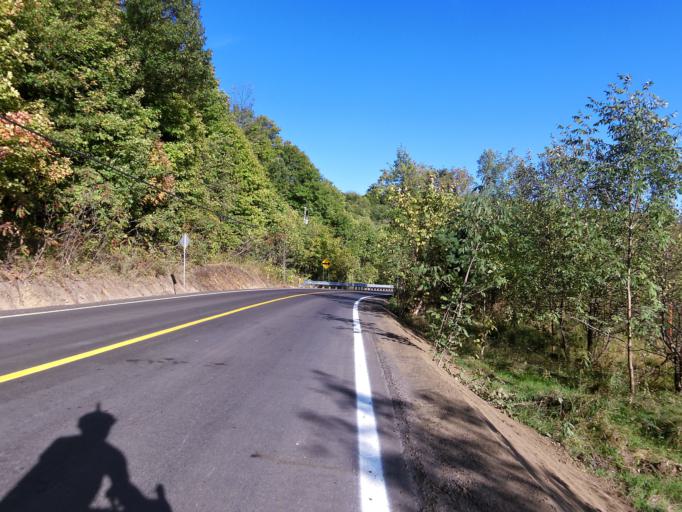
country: CA
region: Quebec
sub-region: Outaouais
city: Wakefield
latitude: 45.4950
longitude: -75.8955
